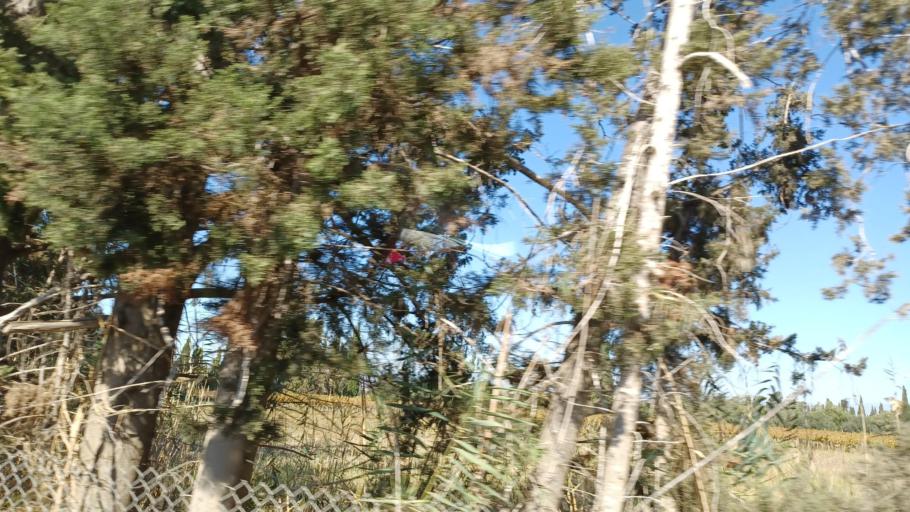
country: CY
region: Larnaka
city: Kolossi
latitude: 34.6273
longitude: 32.9417
